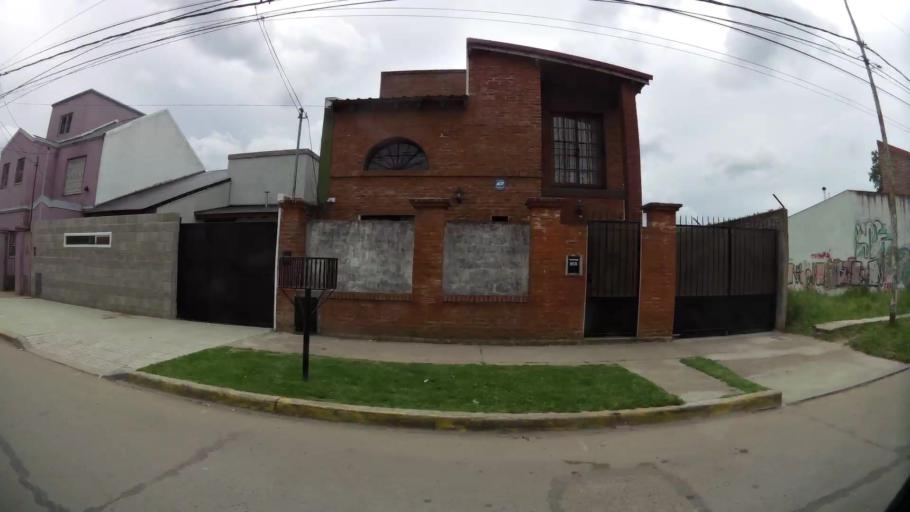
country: AR
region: Buenos Aires
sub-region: Partido de Zarate
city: Zarate
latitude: -34.1147
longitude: -59.0111
